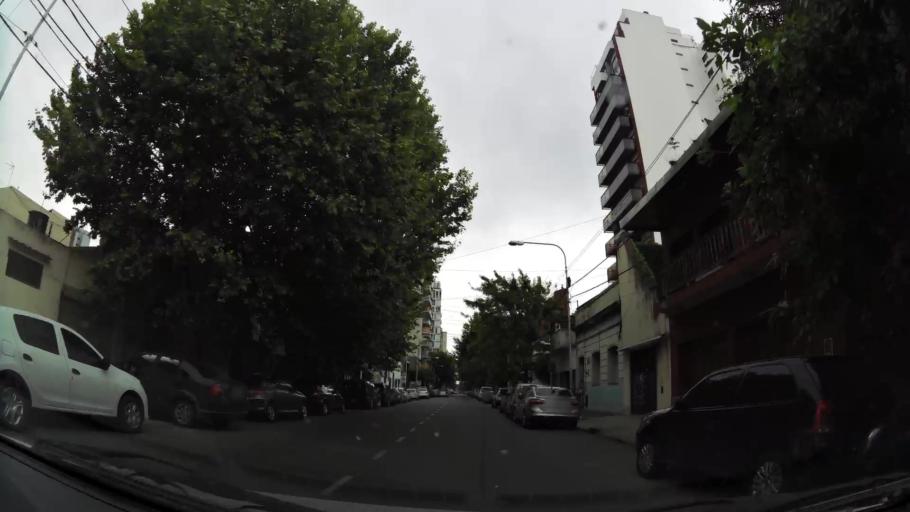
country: AR
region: Buenos Aires
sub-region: Partido de Avellaneda
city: Avellaneda
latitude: -34.6629
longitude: -58.3615
